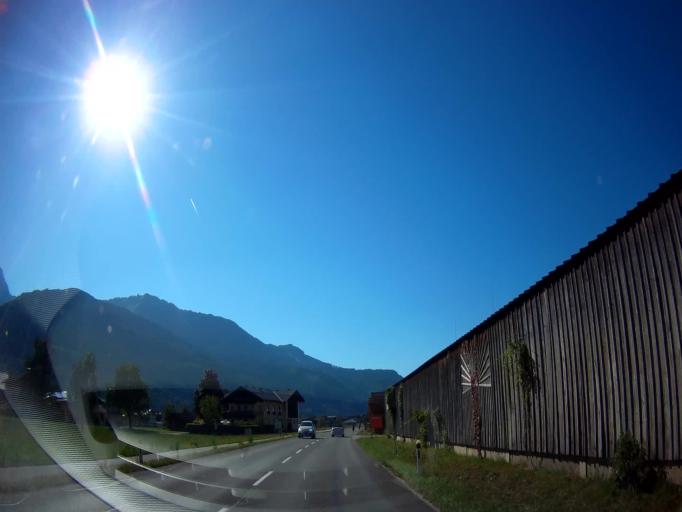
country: AT
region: Salzburg
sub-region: Politischer Bezirk Hallein
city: Kuchl
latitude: 47.6215
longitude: 13.1532
